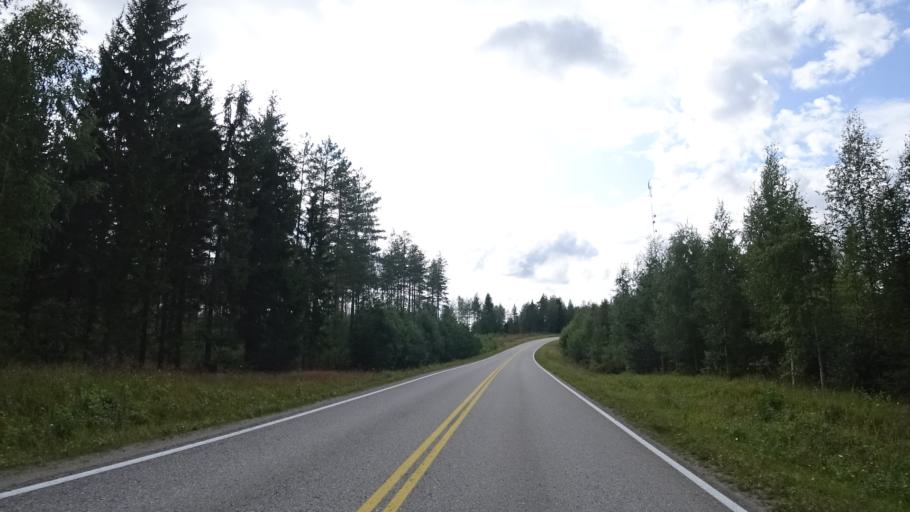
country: FI
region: North Karelia
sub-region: Joensuu
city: Ilomantsi
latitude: 62.7708
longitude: 31.0622
